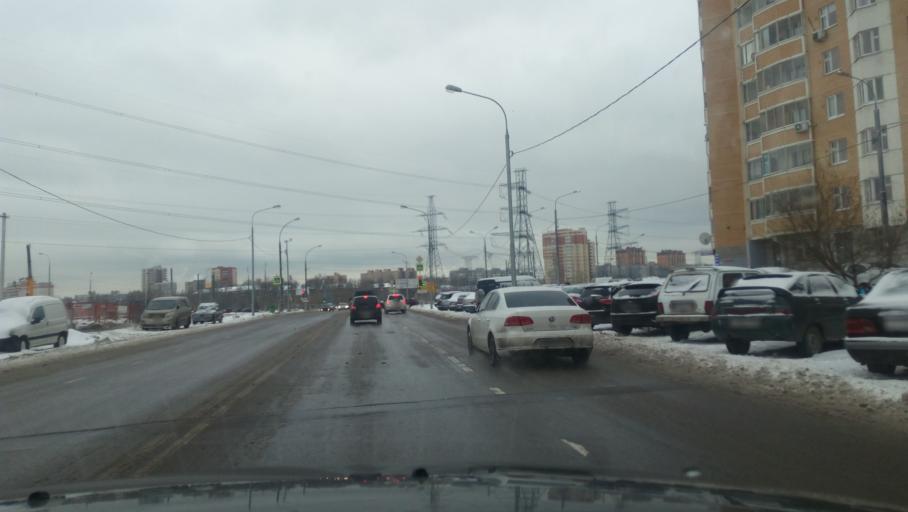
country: RU
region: Moscow
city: Nekrasovka
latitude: 55.7103
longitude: 37.8972
